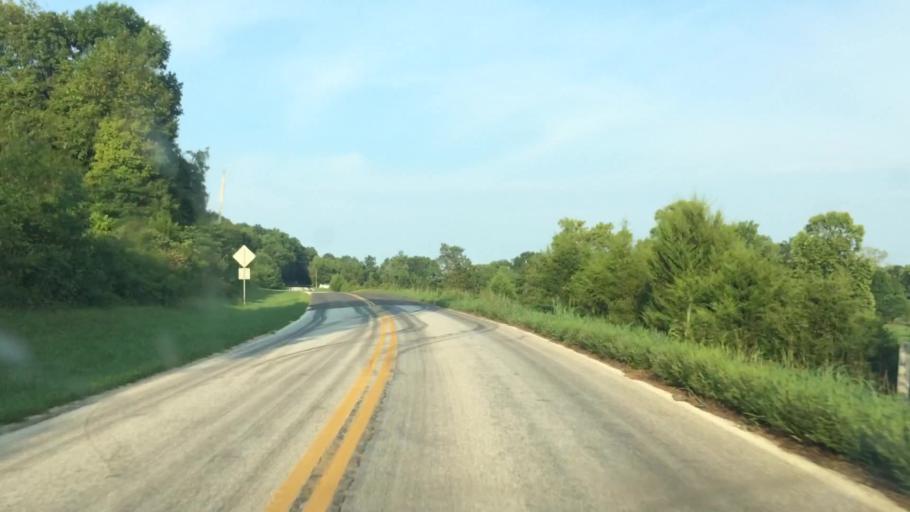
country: US
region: Missouri
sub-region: Greene County
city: Strafford
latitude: 37.1908
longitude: -93.1098
